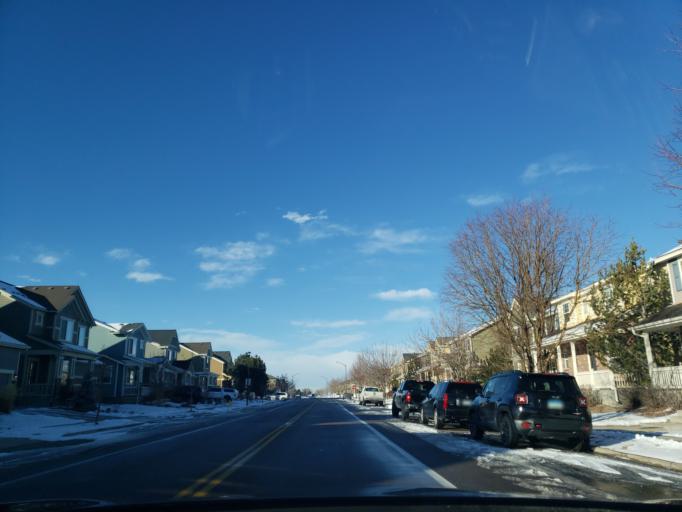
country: US
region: Colorado
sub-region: Larimer County
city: Fort Collins
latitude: 40.5147
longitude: -105.0072
